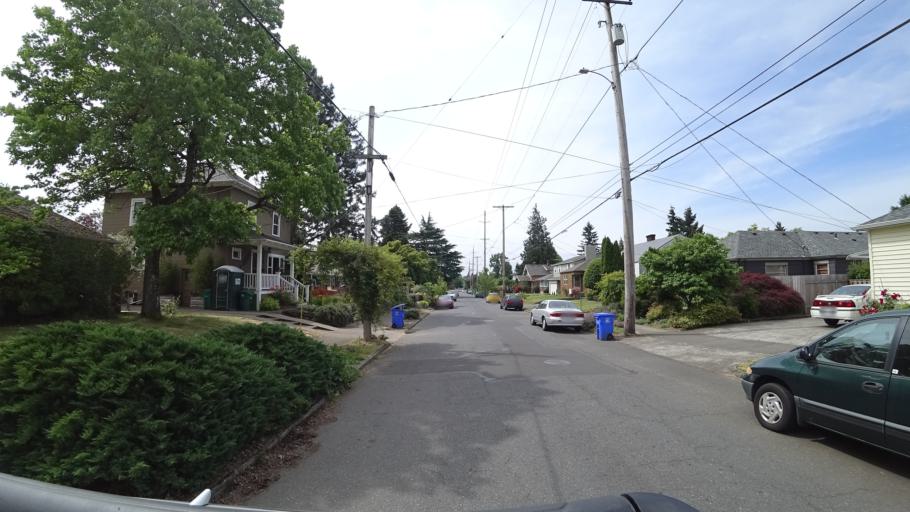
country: US
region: Oregon
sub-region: Multnomah County
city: Lents
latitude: 45.5302
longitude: -122.6088
